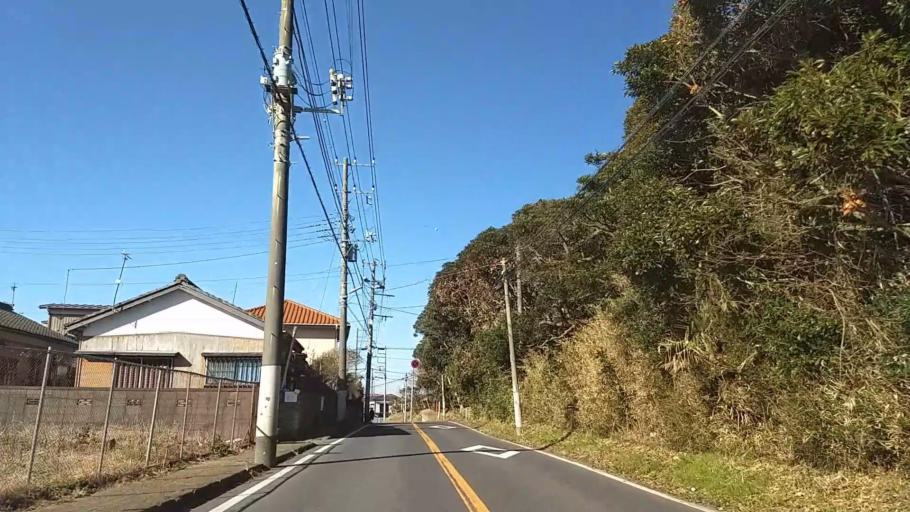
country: JP
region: Chiba
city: Hasaki
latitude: 35.7318
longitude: 140.8550
